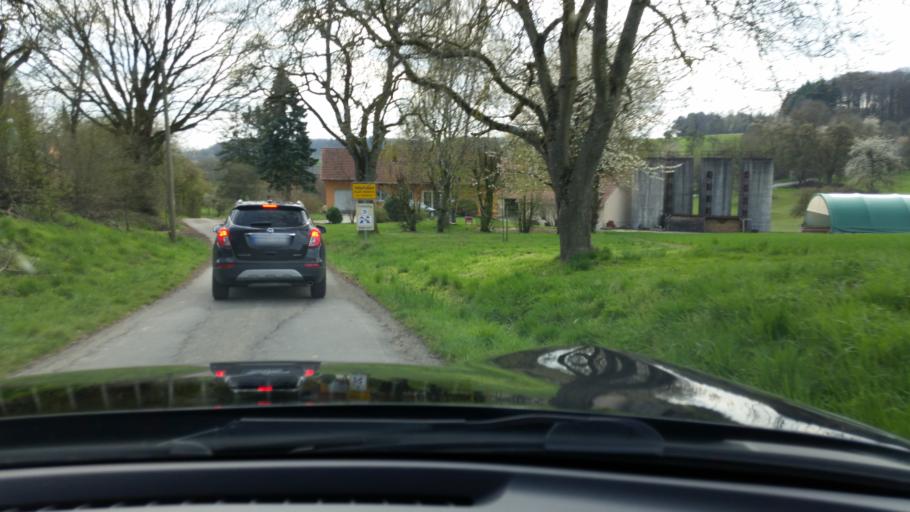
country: DE
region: Baden-Wuerttemberg
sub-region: Regierungsbezirk Stuttgart
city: Widdern
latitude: 49.3564
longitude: 9.4237
